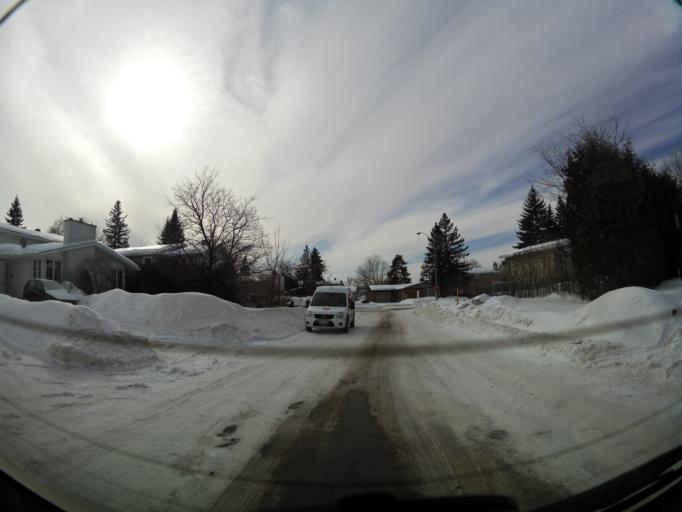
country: CA
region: Ontario
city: Ottawa
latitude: 45.4412
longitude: -75.6002
